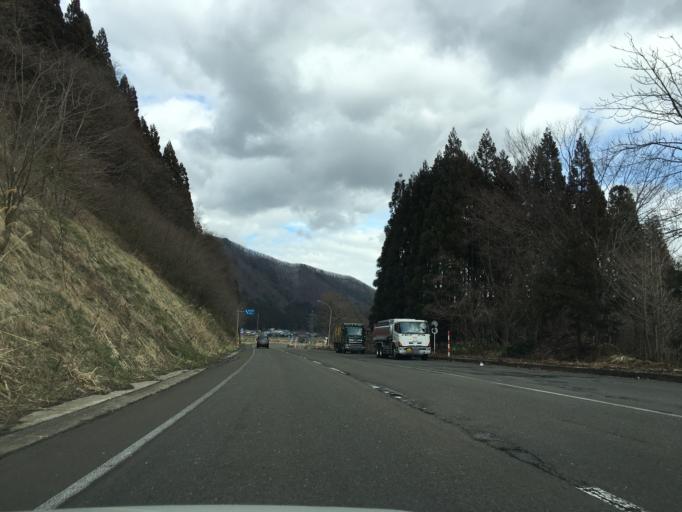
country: JP
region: Akita
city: Odate
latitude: 40.2197
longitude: 140.6488
